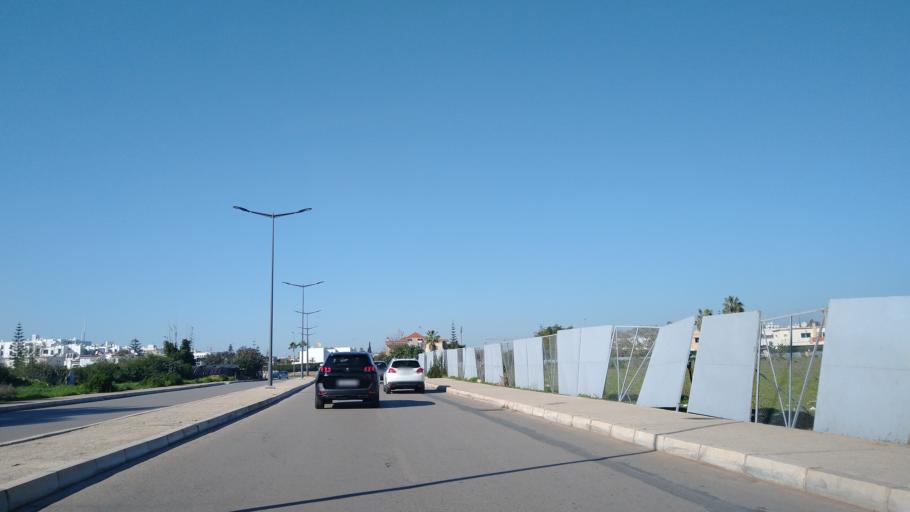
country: MA
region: Rabat-Sale-Zemmour-Zaer
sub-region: Skhirate-Temara
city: Temara
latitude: 33.9544
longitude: -6.8565
